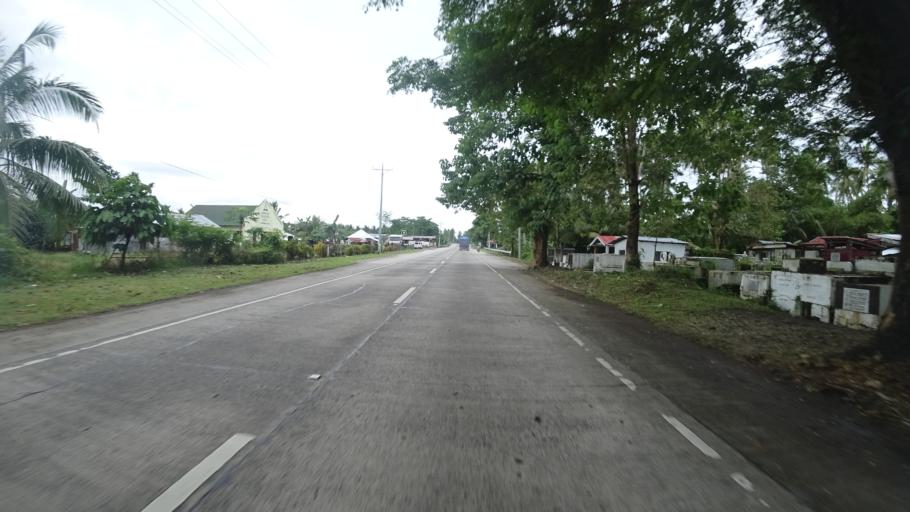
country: PH
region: Eastern Visayas
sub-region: Province of Leyte
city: MacArthur
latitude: 10.8403
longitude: 124.9959
